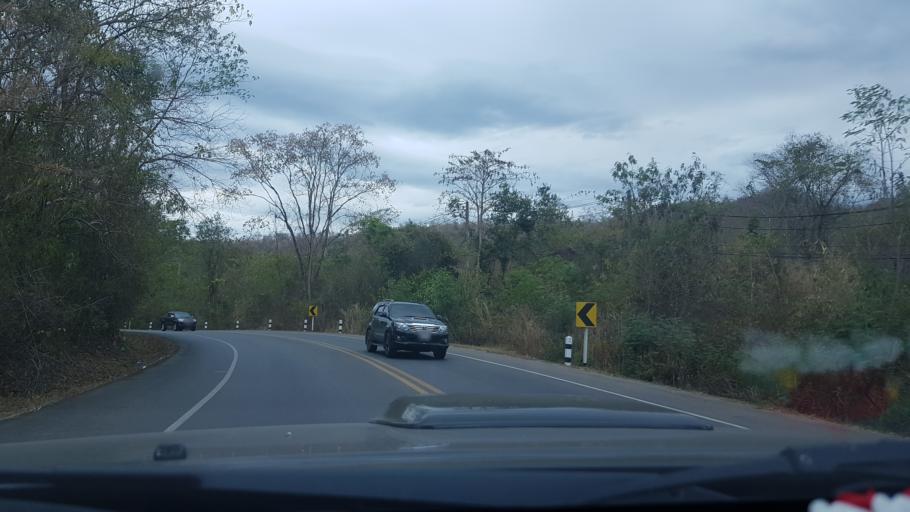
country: TH
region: Phetchabun
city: Phetchabun
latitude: 16.5334
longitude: 101.1082
